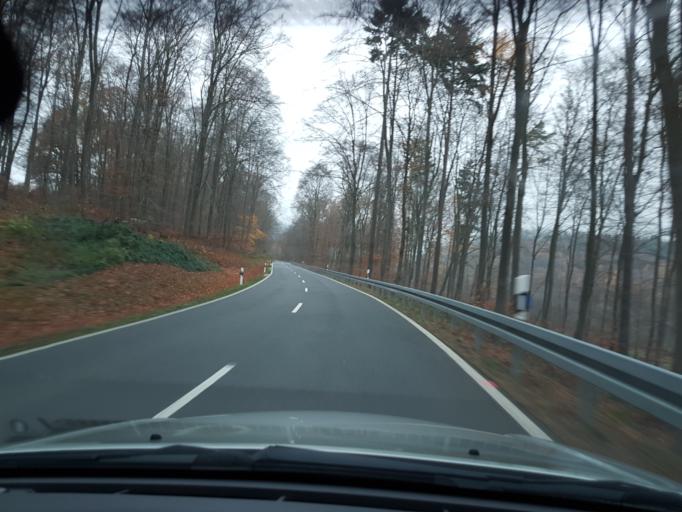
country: DE
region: Hesse
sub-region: Regierungsbezirk Darmstadt
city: Kiedrich
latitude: 50.0608
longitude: 8.0709
